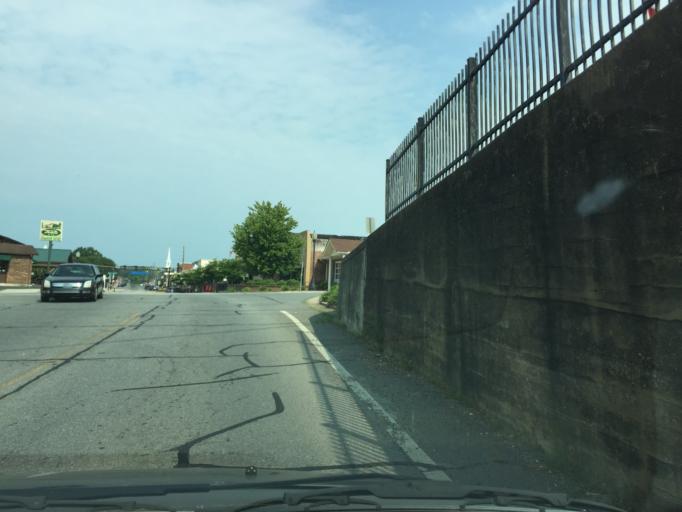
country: US
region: Georgia
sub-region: Catoosa County
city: Ringgold
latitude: 34.9151
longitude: -85.1077
